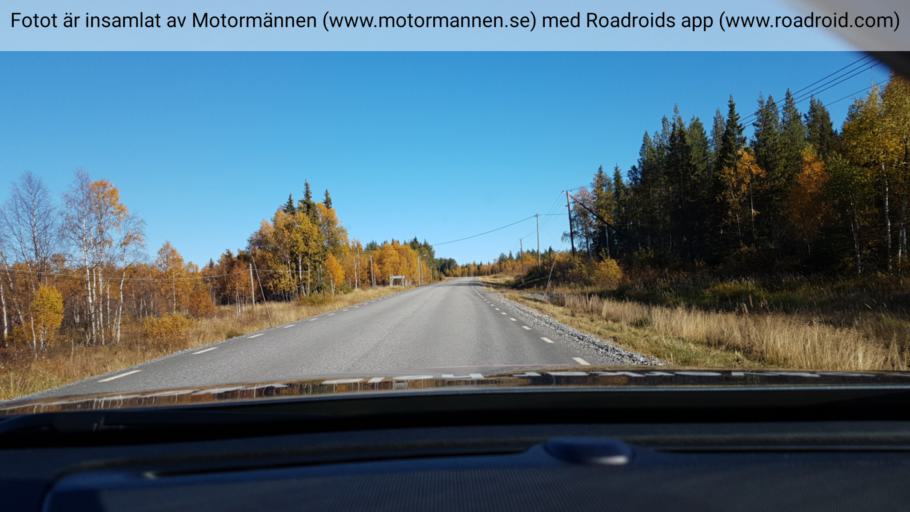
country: SE
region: Norrbotten
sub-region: Gallivare Kommun
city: Gaellivare
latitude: 66.7662
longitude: 21.0371
